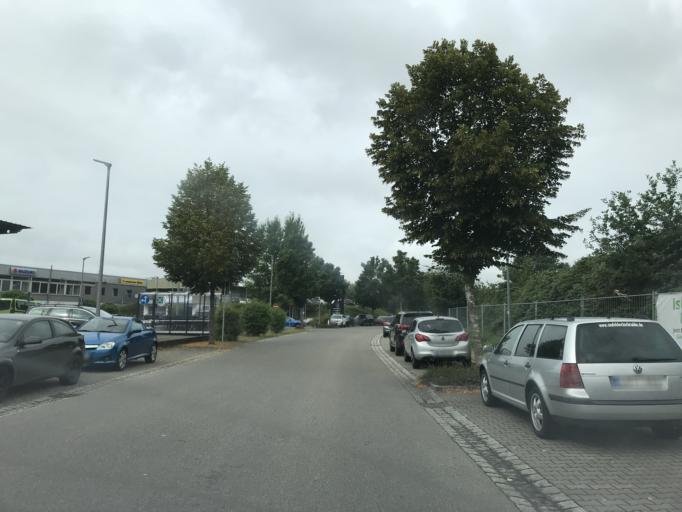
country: DE
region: Baden-Wuerttemberg
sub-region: Freiburg Region
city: Schopfheim
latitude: 47.6486
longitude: 7.8139
